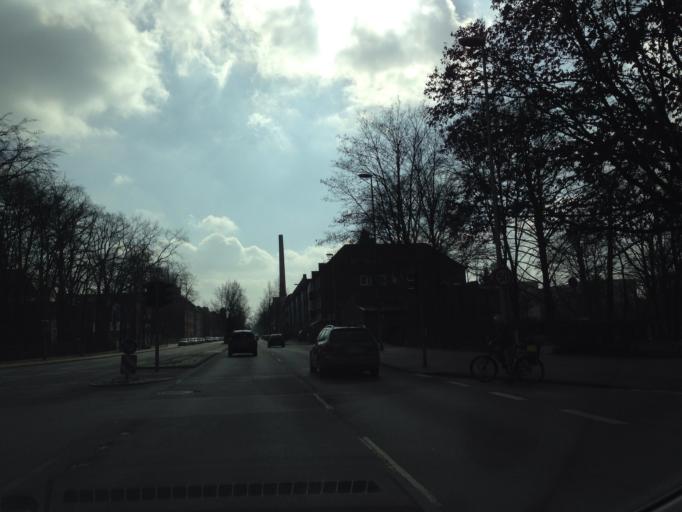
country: DE
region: North Rhine-Westphalia
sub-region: Regierungsbezirk Munster
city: Muenster
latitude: 51.9804
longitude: 7.6120
